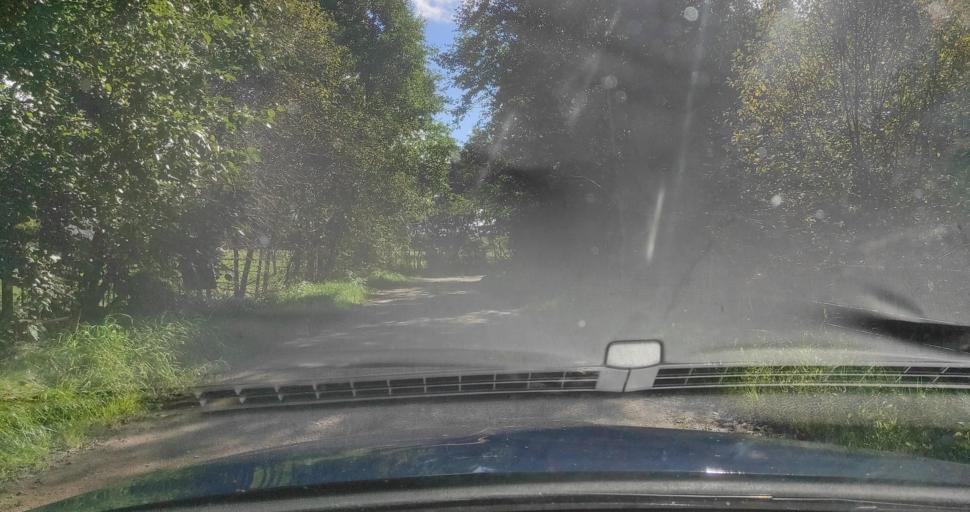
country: LV
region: Ventspils
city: Ventspils
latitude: 57.3689
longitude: 21.6316
